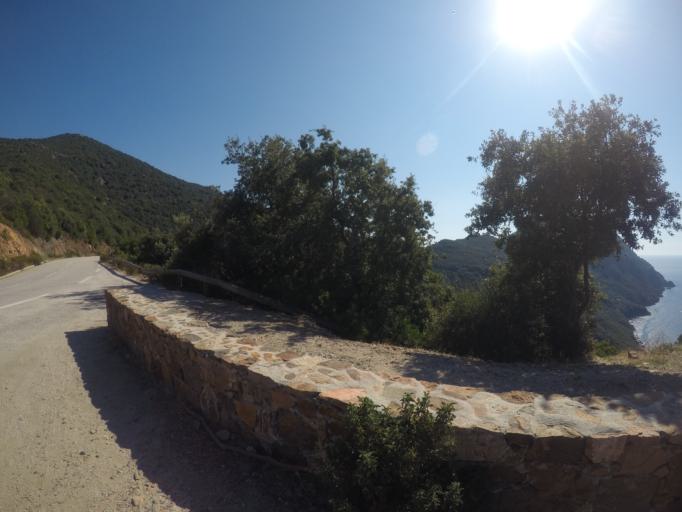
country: FR
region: Corsica
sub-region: Departement de la Corse-du-Sud
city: Cargese
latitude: 42.3349
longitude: 8.6360
